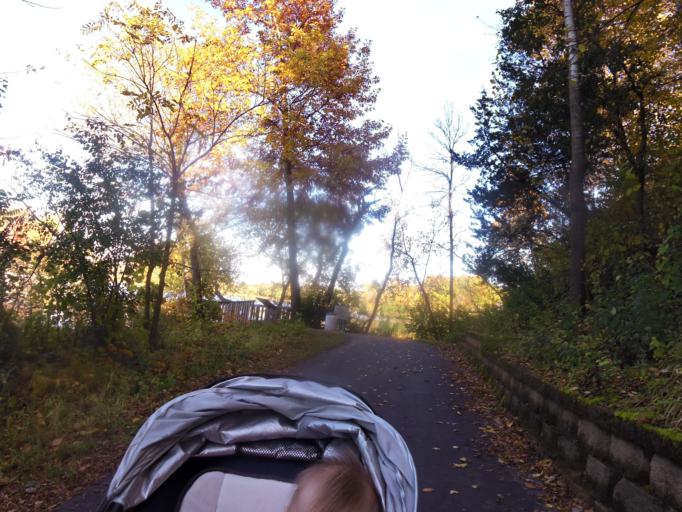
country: US
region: Minnesota
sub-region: Scott County
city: Prior Lake
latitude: 44.7002
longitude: -93.4409
